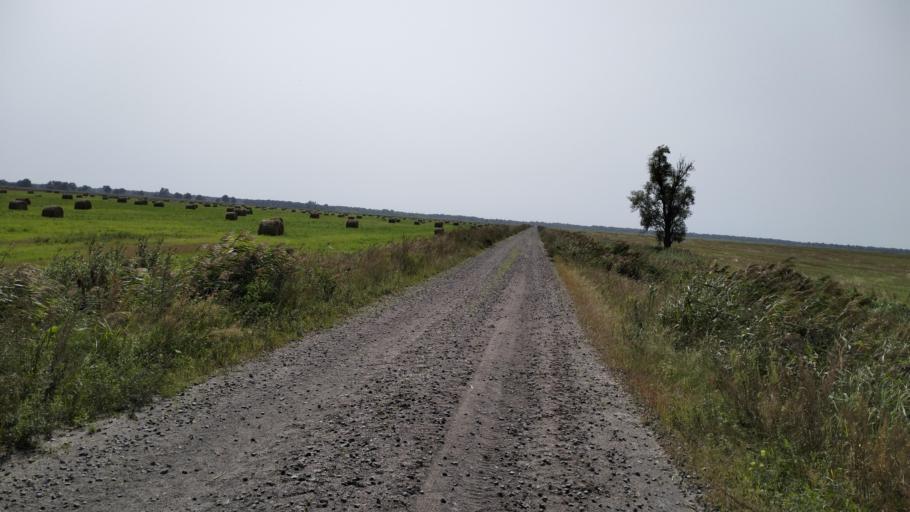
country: BY
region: Brest
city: Davyd-Haradok
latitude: 51.9941
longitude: 27.1763
